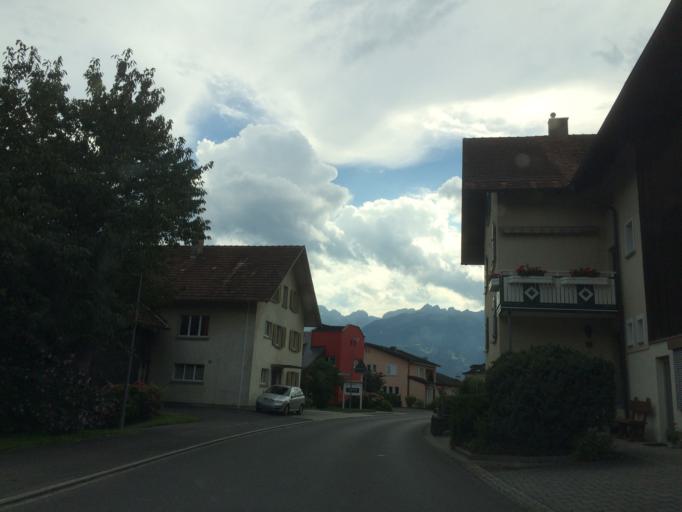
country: LI
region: Eschen
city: Eschen
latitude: 47.2115
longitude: 9.5205
